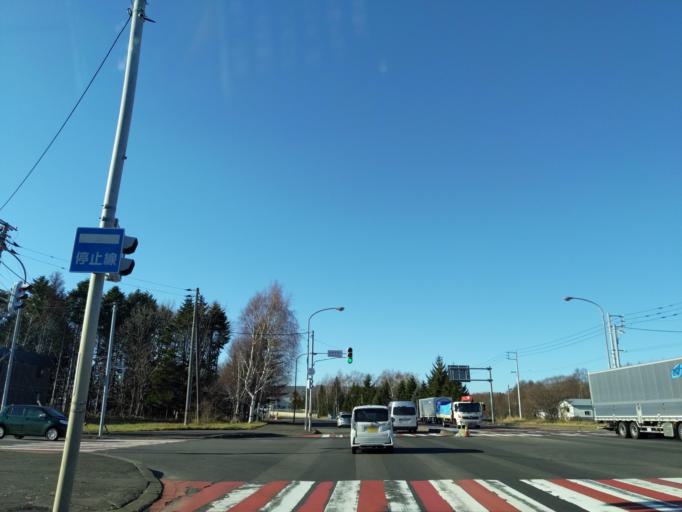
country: JP
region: Hokkaido
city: Kitahiroshima
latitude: 42.9055
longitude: 141.5607
